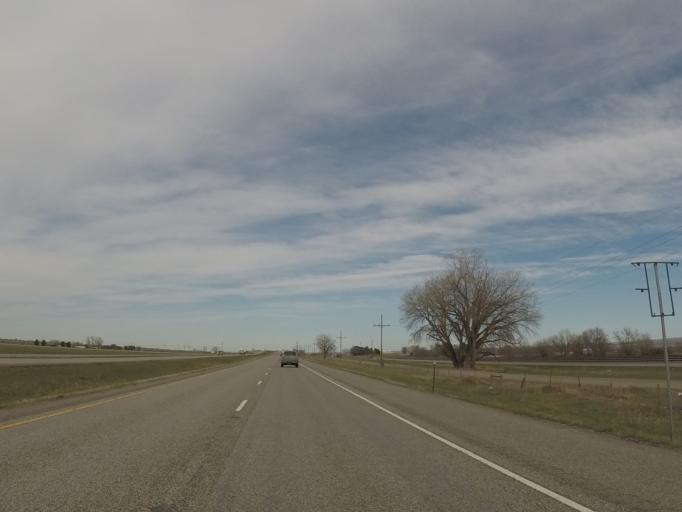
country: US
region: Montana
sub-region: Yellowstone County
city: Laurel
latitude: 45.6543
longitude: -108.8329
